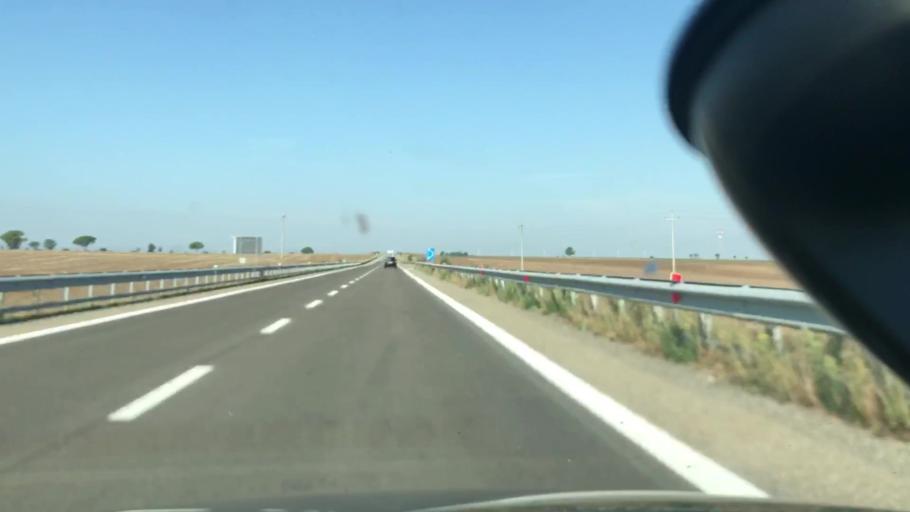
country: IT
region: Basilicate
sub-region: Provincia di Potenza
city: Montemilone
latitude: 40.9881
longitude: 15.9077
